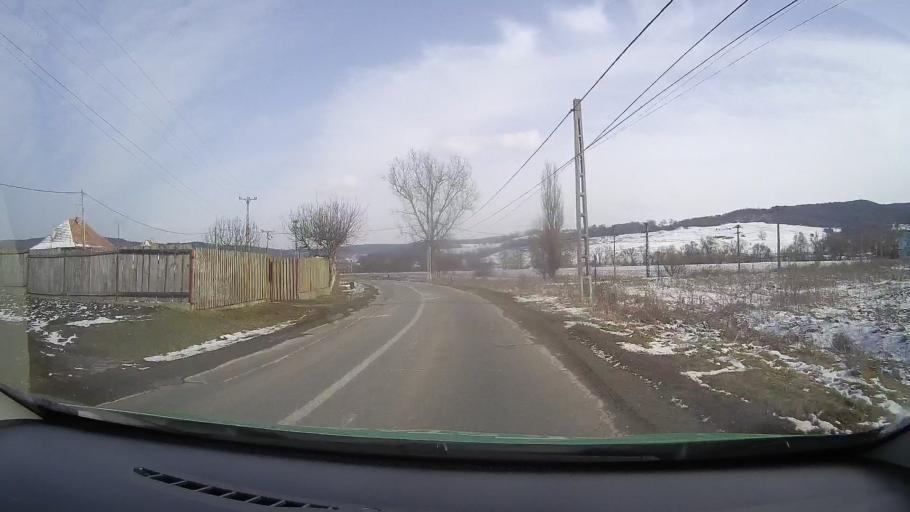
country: RO
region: Mures
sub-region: Comuna Apold
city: Saes
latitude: 46.1408
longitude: 24.7887
